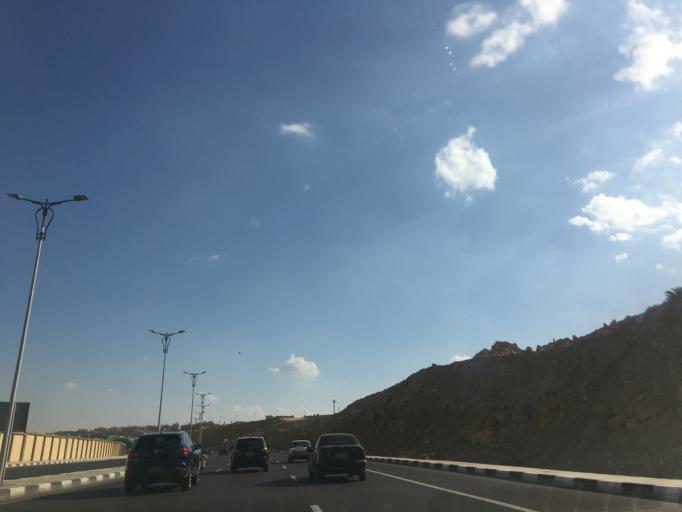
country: EG
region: Muhafazat al Qahirah
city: Cairo
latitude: 30.0308
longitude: 31.3092
